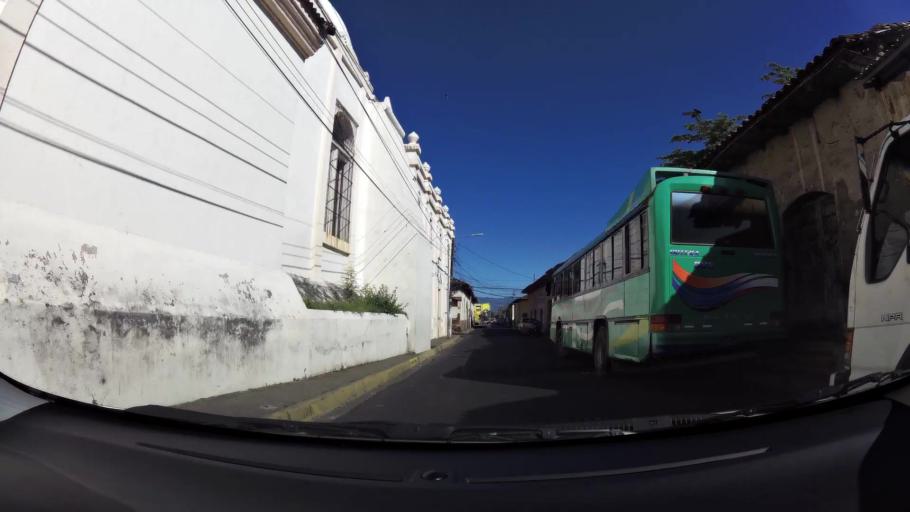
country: SV
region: San Miguel
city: San Miguel
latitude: 13.4854
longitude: -88.1764
